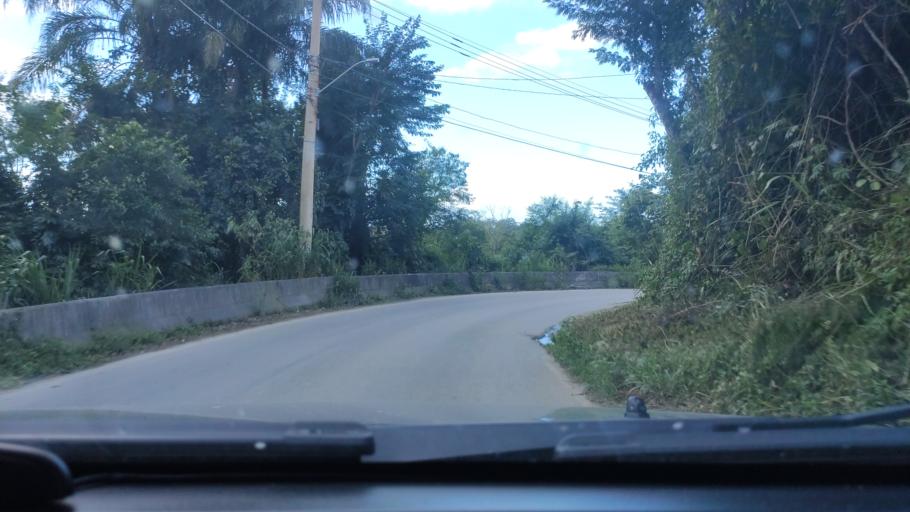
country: BR
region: Sao Paulo
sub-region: Sao Sebastiao
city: Sao Sebastiao
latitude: -23.6986
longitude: -45.4826
